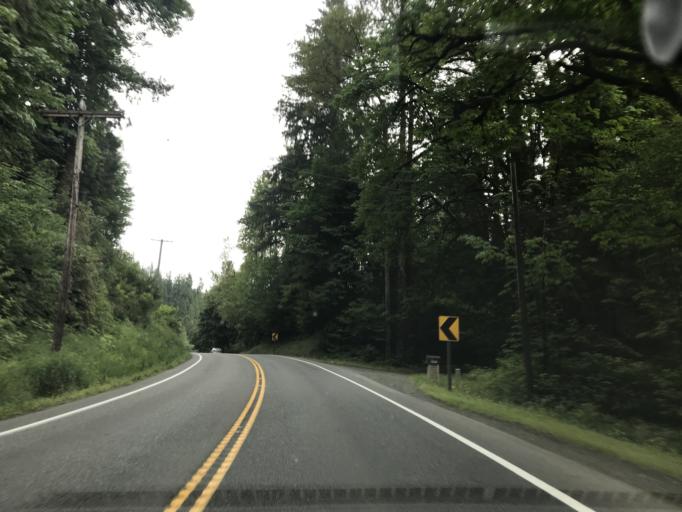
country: US
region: Washington
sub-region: King County
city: Fall City
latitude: 47.5449
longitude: -121.9033
